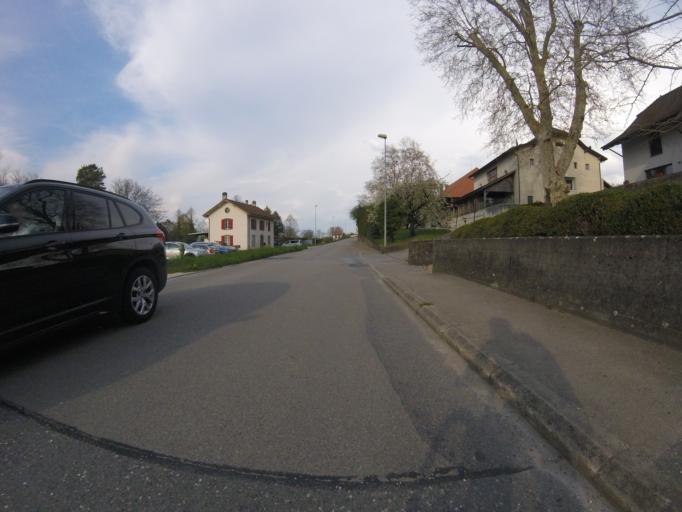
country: CH
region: Fribourg
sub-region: See District
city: Gurwolf
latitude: 46.9078
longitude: 7.0742
